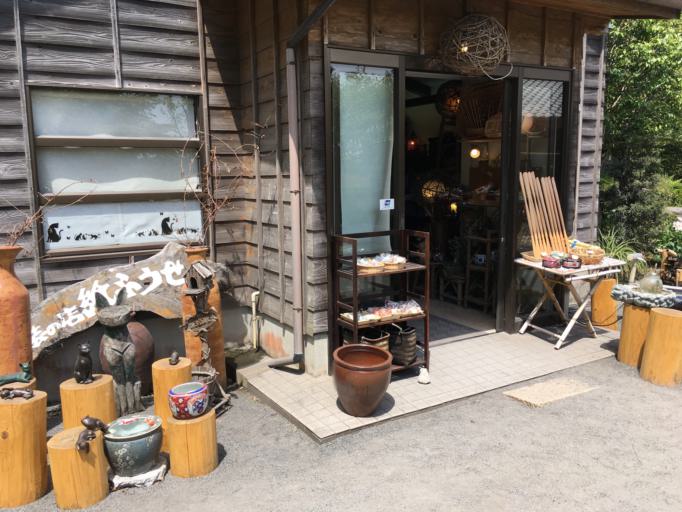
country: JP
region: Kagoshima
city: Kagoshima-shi
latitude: 31.6194
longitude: 130.5800
